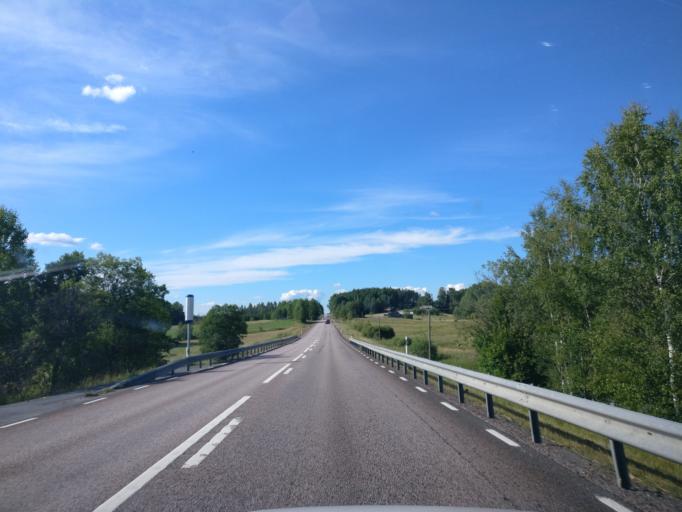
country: SE
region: Vaermland
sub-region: Karlstads Kommun
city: Edsvalla
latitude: 59.5777
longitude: 13.0187
